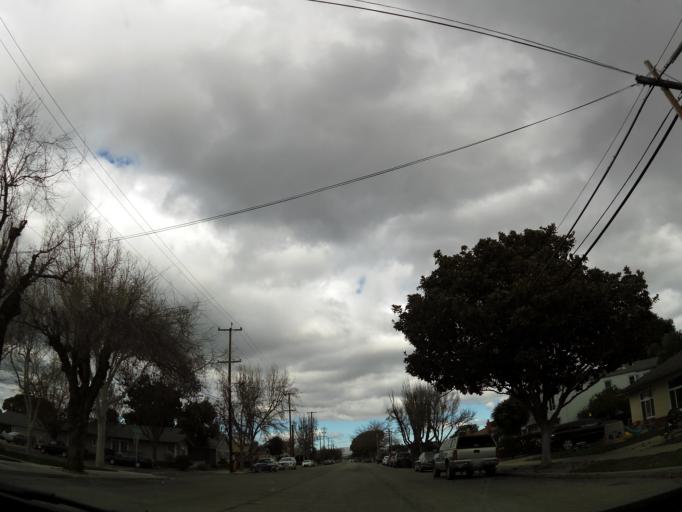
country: US
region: California
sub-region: San Benito County
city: Hollister
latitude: 36.8411
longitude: -121.4004
